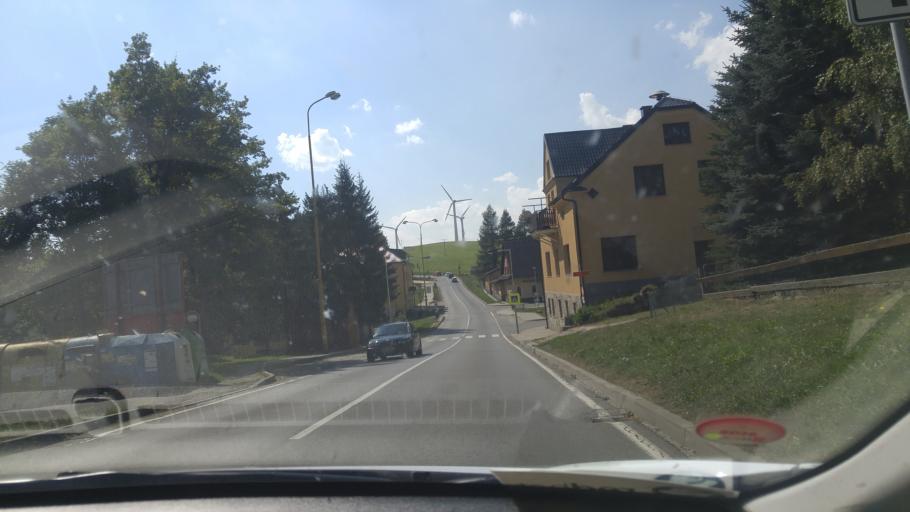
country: CZ
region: Olomoucky
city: Vapenna
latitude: 50.1857
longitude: 17.0526
